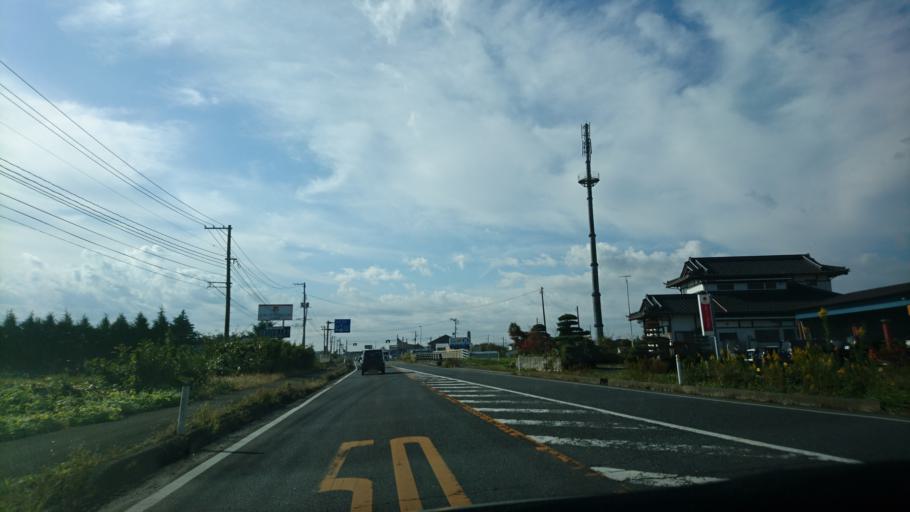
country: JP
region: Miyagi
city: Furukawa
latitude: 38.6174
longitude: 140.9840
